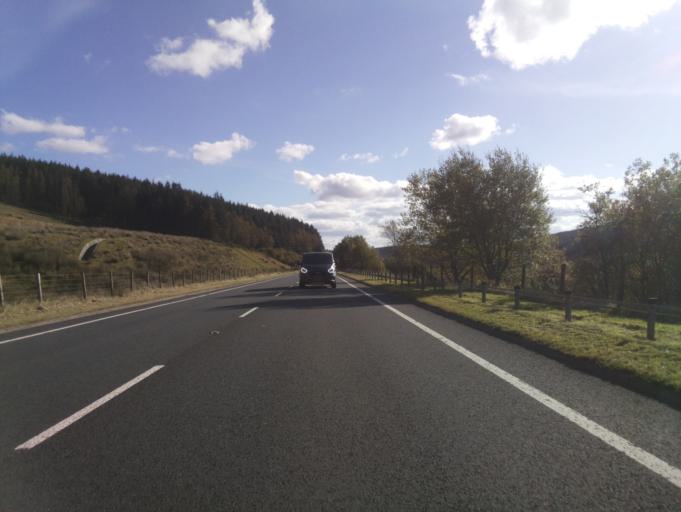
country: GB
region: Wales
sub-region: Rhondda Cynon Taf
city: Hirwaun
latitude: 51.8471
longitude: -3.4656
